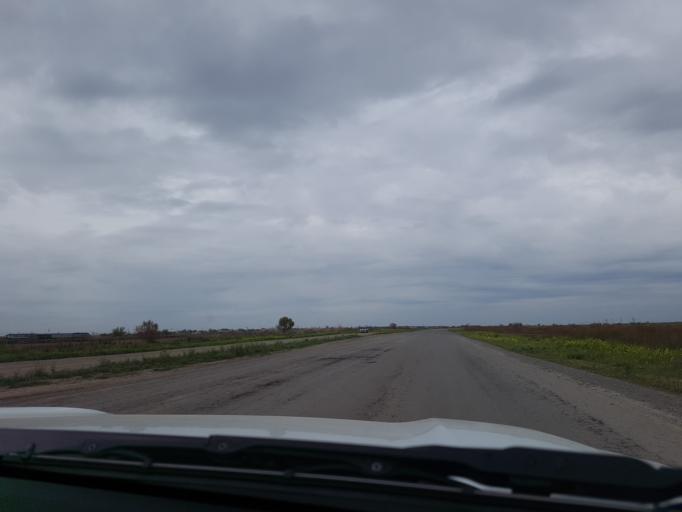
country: TM
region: Mary
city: Bayramaly
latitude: 37.7882
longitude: 62.5467
